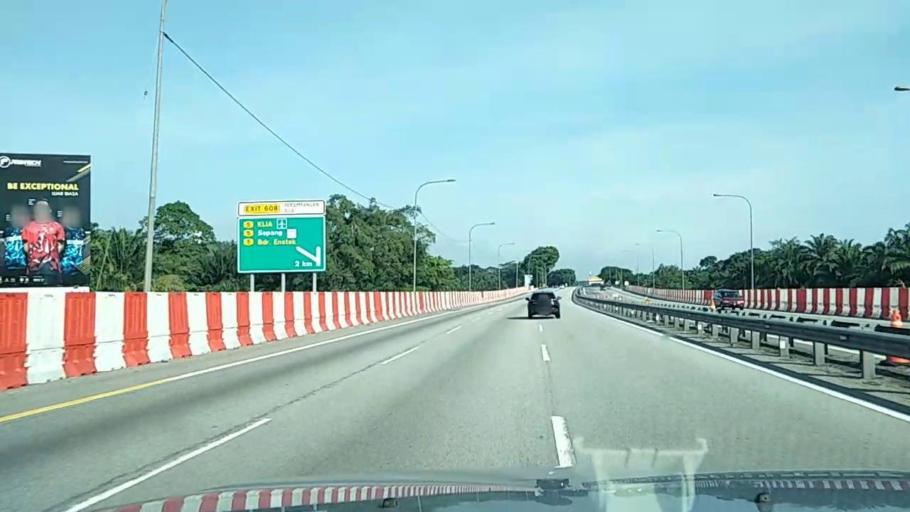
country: MY
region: Putrajaya
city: Putrajaya
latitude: 2.8457
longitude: 101.6828
